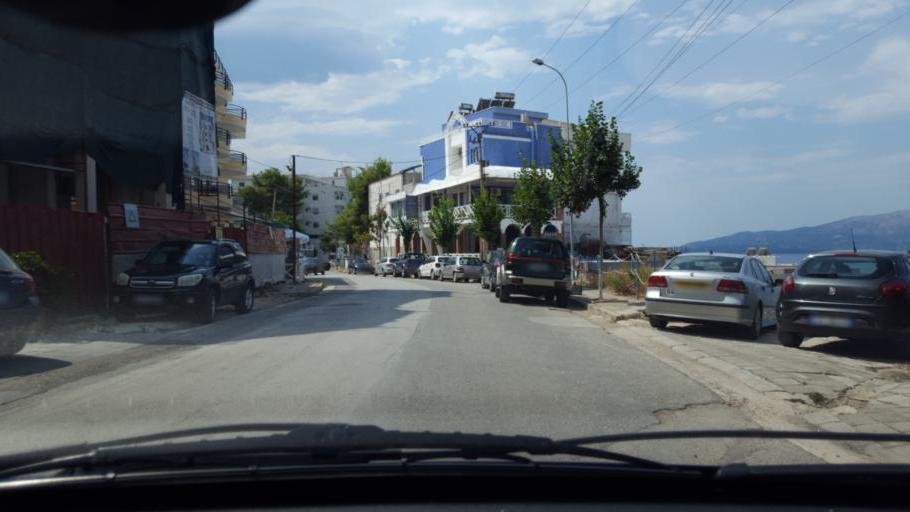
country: AL
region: Vlore
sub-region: Rrethi i Sarandes
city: Sarande
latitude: 39.8532
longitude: 20.0228
